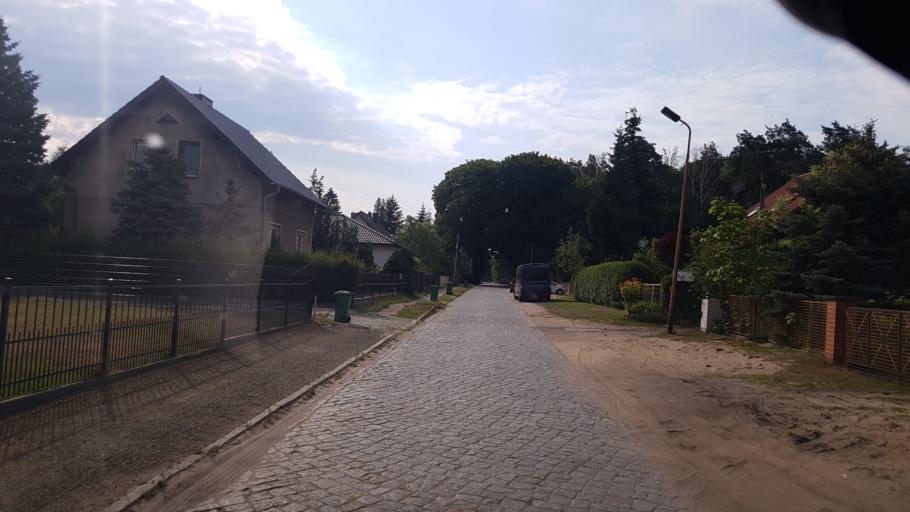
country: DE
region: Brandenburg
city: Gross Koris
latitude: 52.1667
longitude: 13.6895
